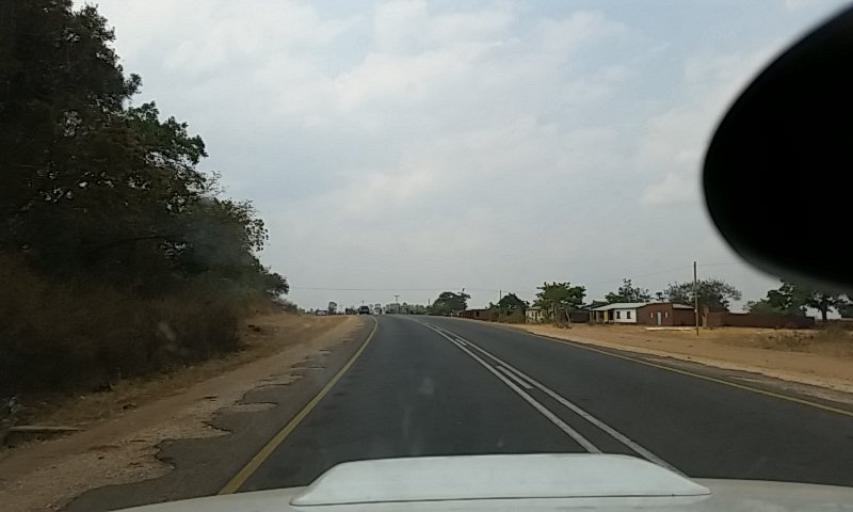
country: MW
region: Central Region
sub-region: Lilongwe District
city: Lilongwe
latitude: -13.8375
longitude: 33.8517
